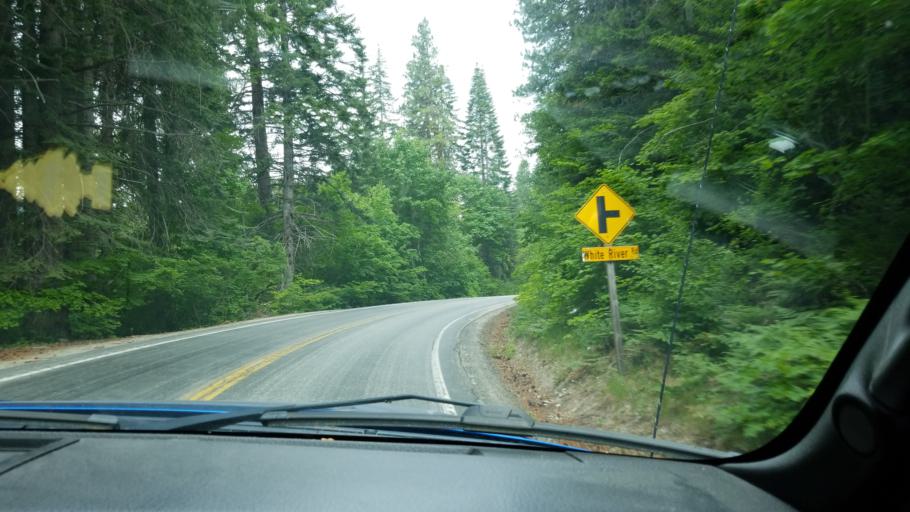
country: US
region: Washington
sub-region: Chelan County
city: Leavenworth
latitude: 47.8494
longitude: -120.8304
